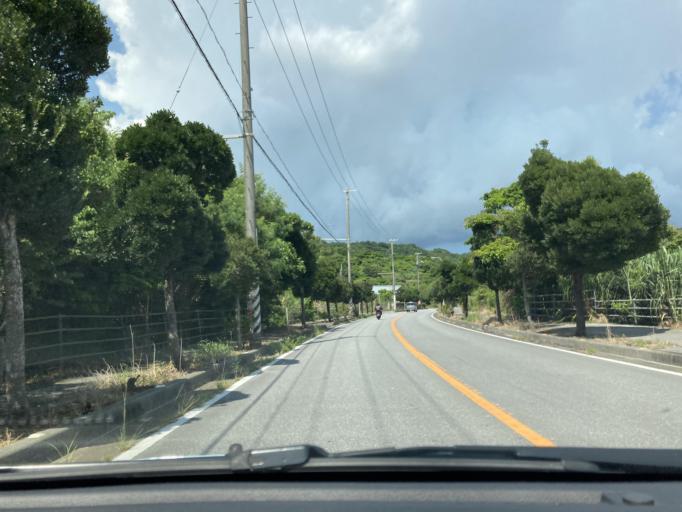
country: JP
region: Okinawa
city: Tomigusuku
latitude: 26.1728
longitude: 127.7696
